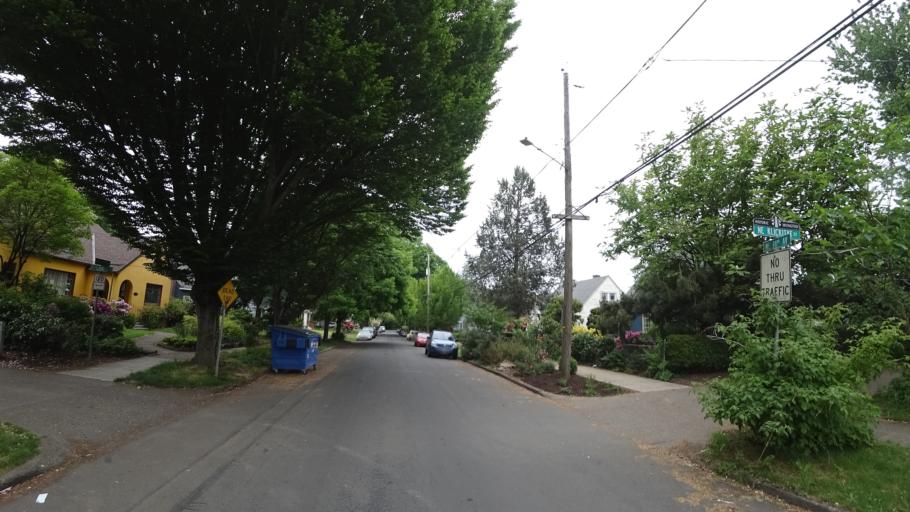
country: US
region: Oregon
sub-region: Multnomah County
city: Portland
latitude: 45.5467
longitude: -122.6545
